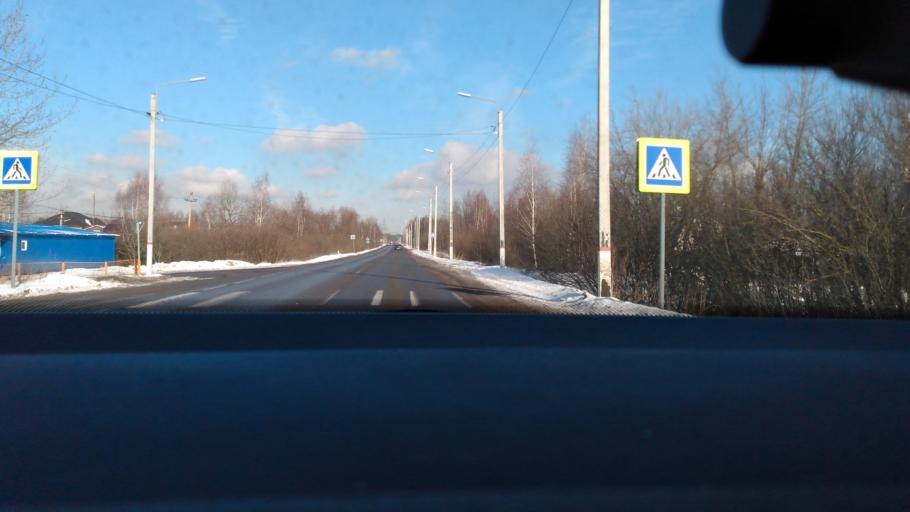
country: RU
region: Moskovskaya
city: Kratovo
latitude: 55.6254
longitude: 38.1581
